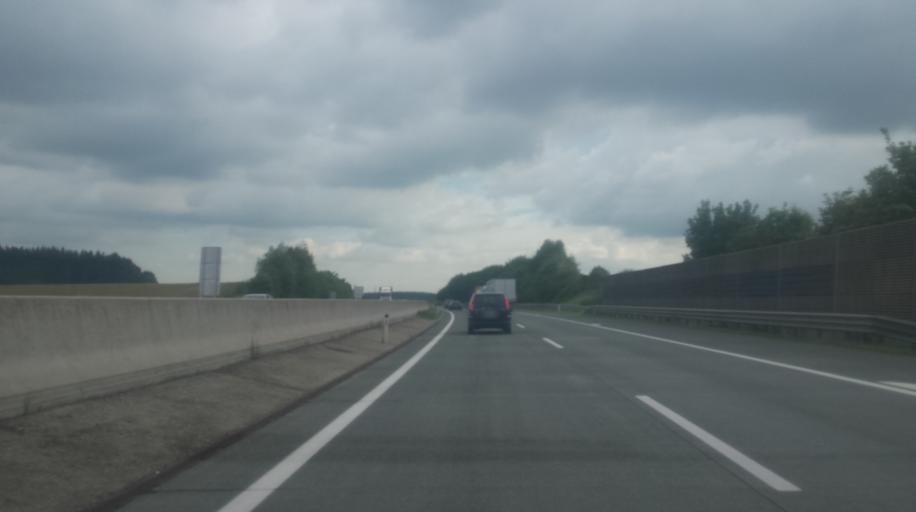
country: AT
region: Upper Austria
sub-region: Politischer Bezirk Vocklabruck
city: Desselbrunn
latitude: 47.9683
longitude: 13.7644
